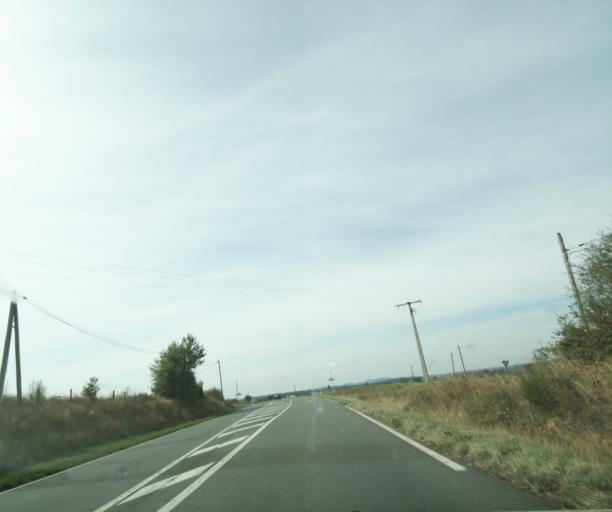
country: FR
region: Auvergne
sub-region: Departement de l'Allier
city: Saint-Francois
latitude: 46.3750
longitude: 3.8660
